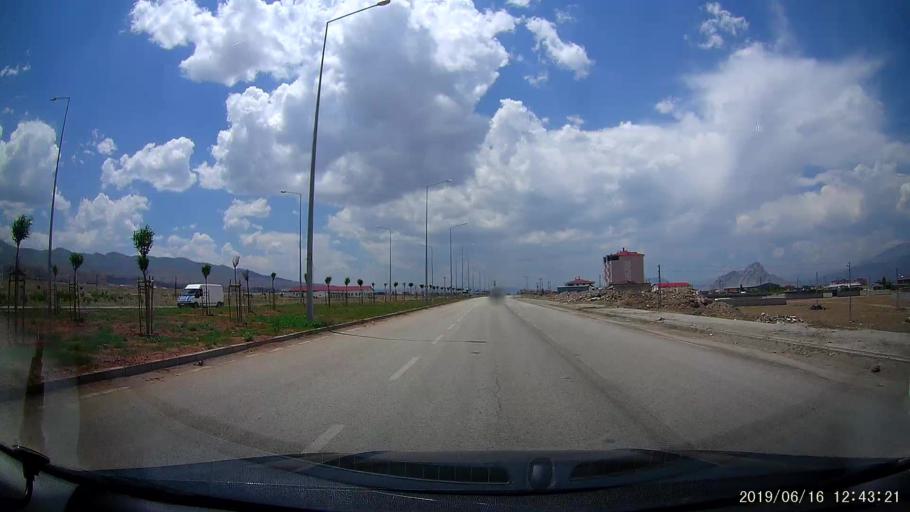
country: TR
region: Agri
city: Dogubayazit
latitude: 39.5580
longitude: 44.1186
